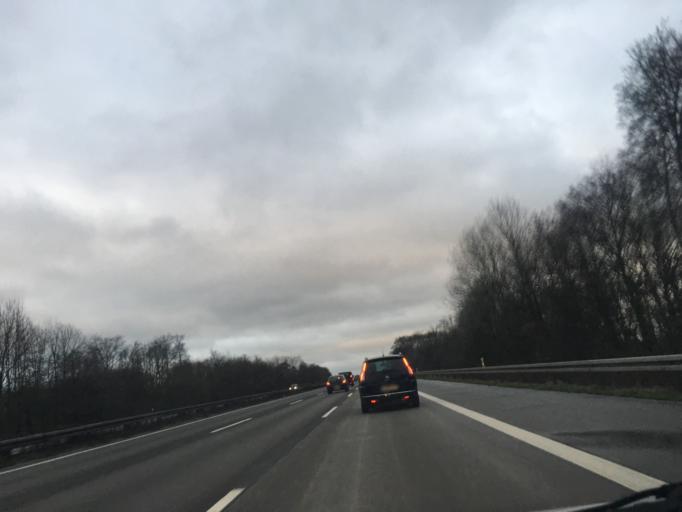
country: DE
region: North Rhine-Westphalia
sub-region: Regierungsbezirk Dusseldorf
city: Ratingen
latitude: 51.3344
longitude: 6.8792
